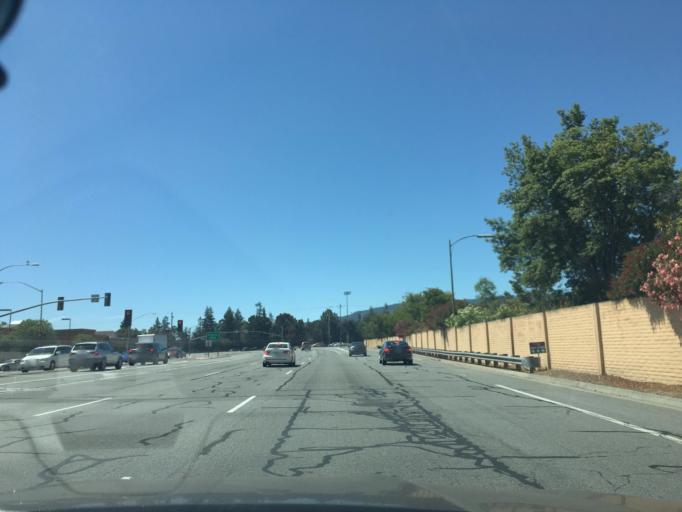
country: US
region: California
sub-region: Santa Clara County
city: Saratoga
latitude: 37.2945
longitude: -121.9976
